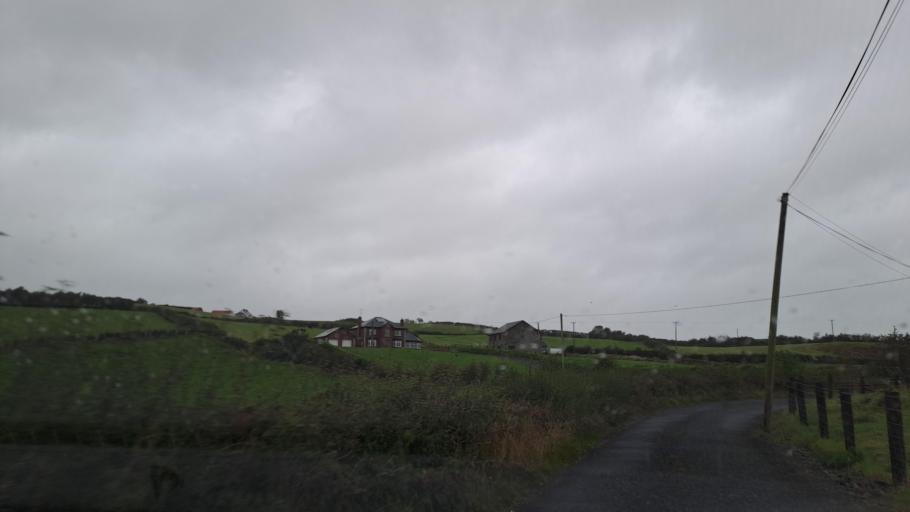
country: IE
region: Ulster
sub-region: An Cabhan
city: Kingscourt
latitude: 54.0072
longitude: -6.8395
